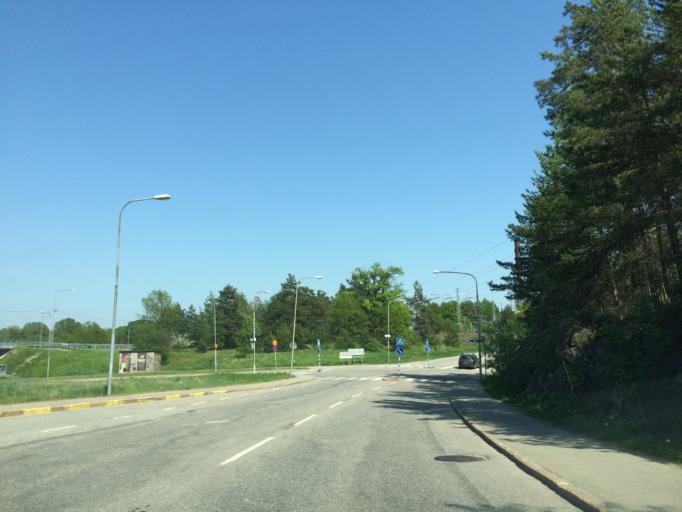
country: SE
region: Stockholm
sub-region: Nacka Kommun
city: Alta
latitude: 59.2639
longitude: 18.1423
